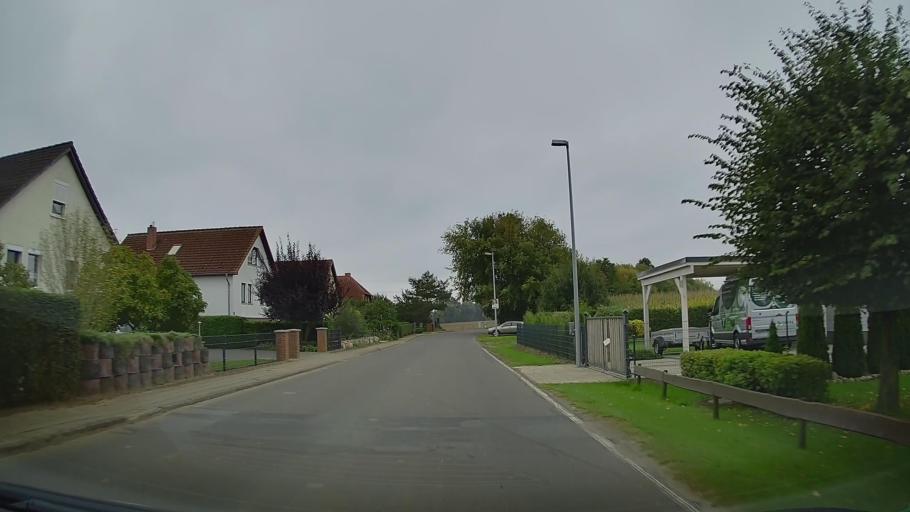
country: DE
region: Mecklenburg-Vorpommern
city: Guestrow
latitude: 53.8098
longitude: 12.1138
